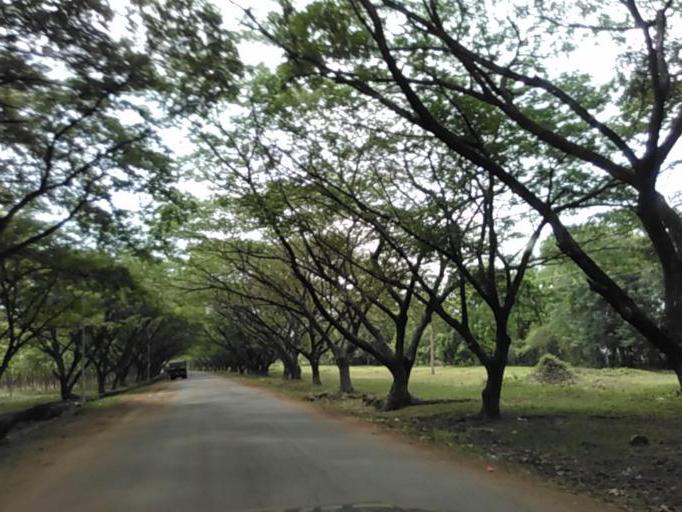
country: GH
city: Akropong
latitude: 6.0950
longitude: 0.1104
